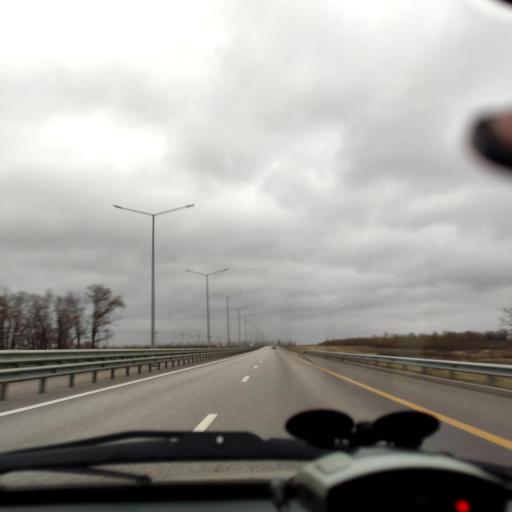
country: RU
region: Voronezj
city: Podkletnoye
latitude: 51.5889
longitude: 39.4240
